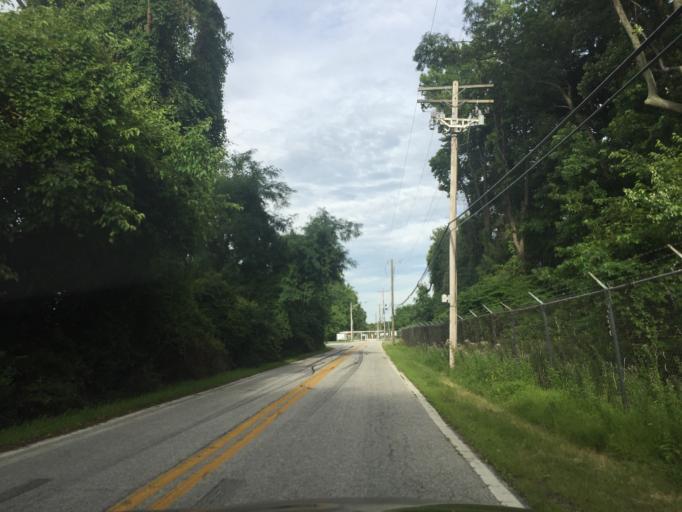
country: US
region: Maryland
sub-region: Baltimore County
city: Bowleys Quarters
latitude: 39.3275
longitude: -76.3669
